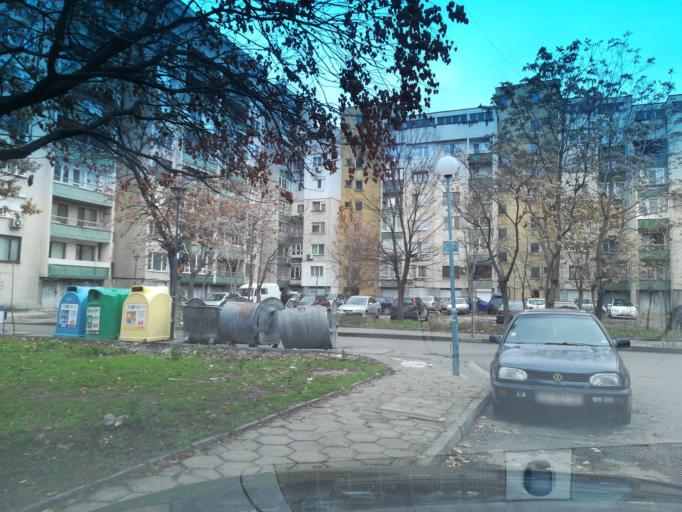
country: BG
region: Plovdiv
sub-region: Obshtina Plovdiv
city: Plovdiv
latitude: 42.1494
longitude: 24.7624
